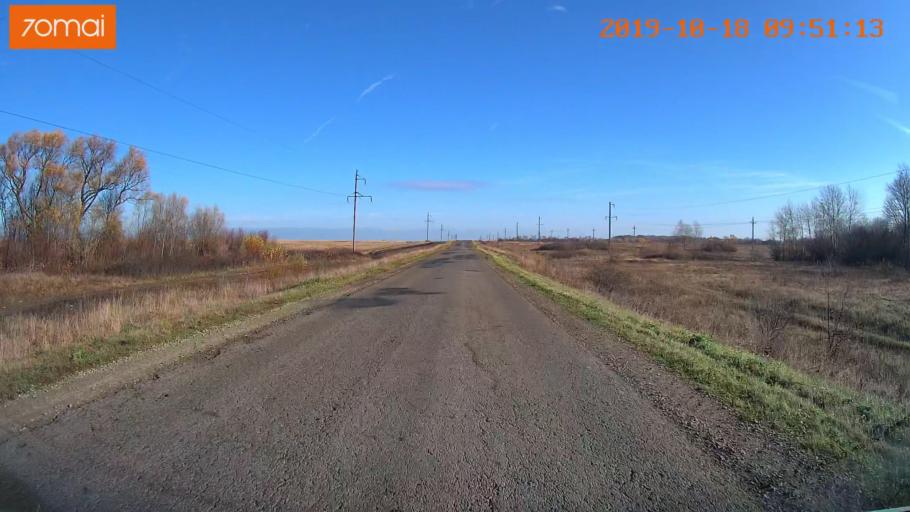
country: RU
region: Tula
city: Kazachka
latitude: 53.3379
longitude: 38.2891
